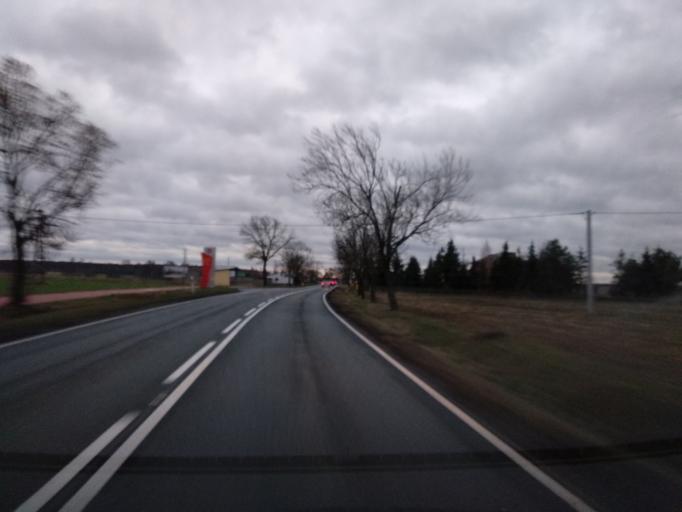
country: PL
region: Greater Poland Voivodeship
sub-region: Powiat koninski
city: Rychwal
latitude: 52.1040
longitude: 18.1674
